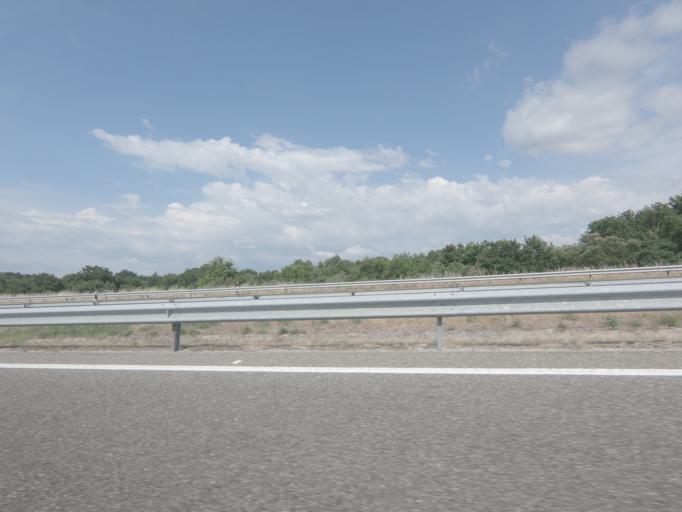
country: ES
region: Galicia
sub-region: Provincia de Ourense
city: Taboadela
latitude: 42.2633
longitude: -7.8686
